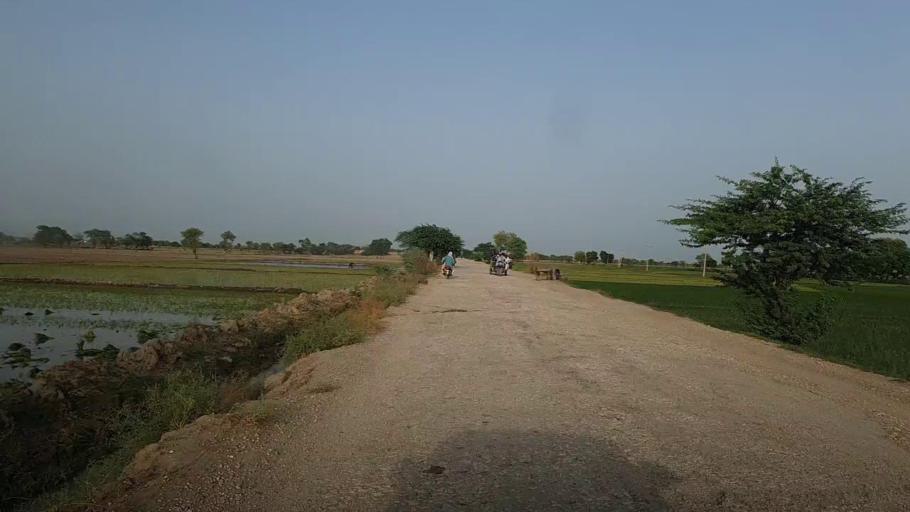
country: PK
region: Sindh
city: Mehar
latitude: 27.1645
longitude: 67.7830
